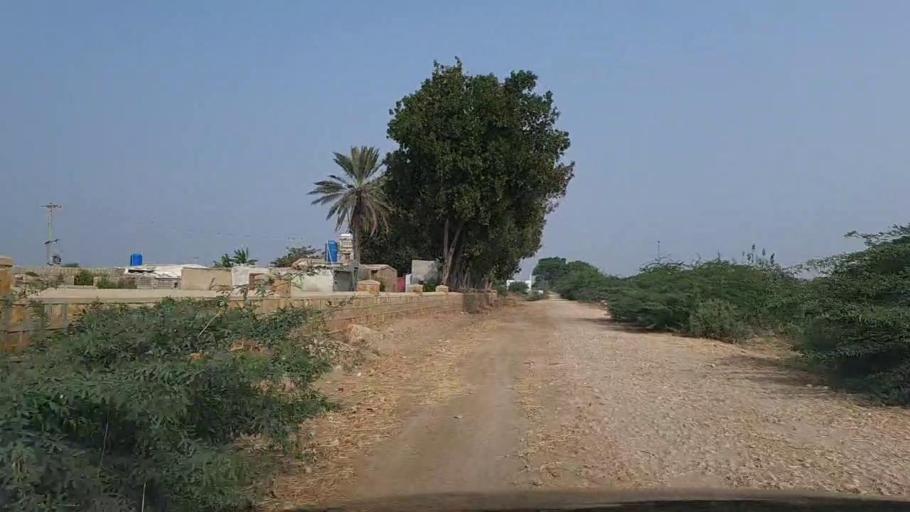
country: PK
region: Sindh
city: Thatta
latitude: 24.7667
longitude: 67.8709
